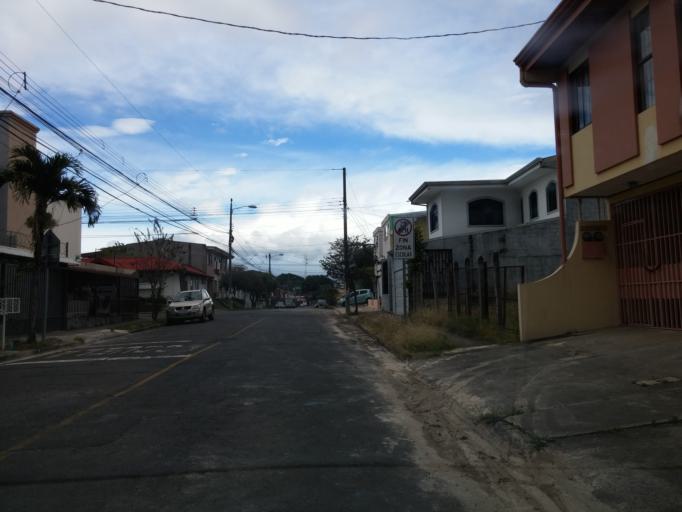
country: CR
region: San Jose
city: San Jose
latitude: 9.9276
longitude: -84.0997
